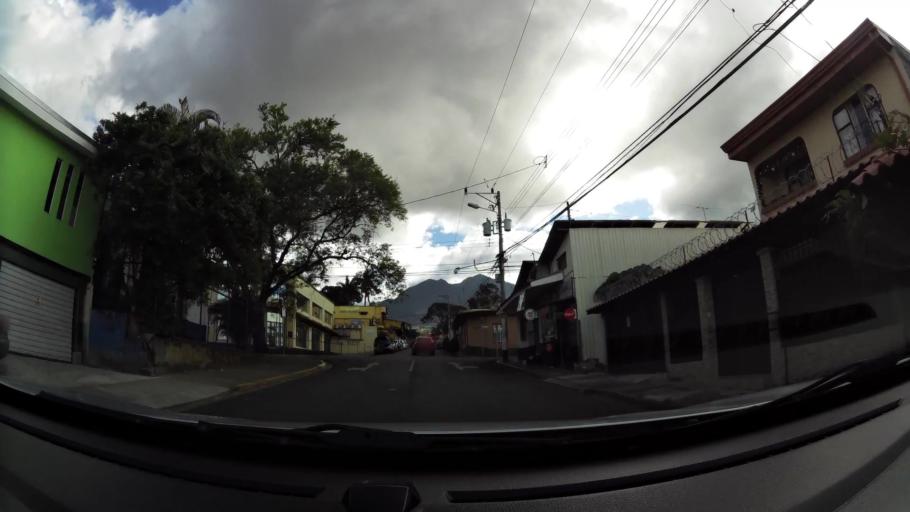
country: CR
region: San Jose
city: Escazu
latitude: 9.9214
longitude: -84.1399
